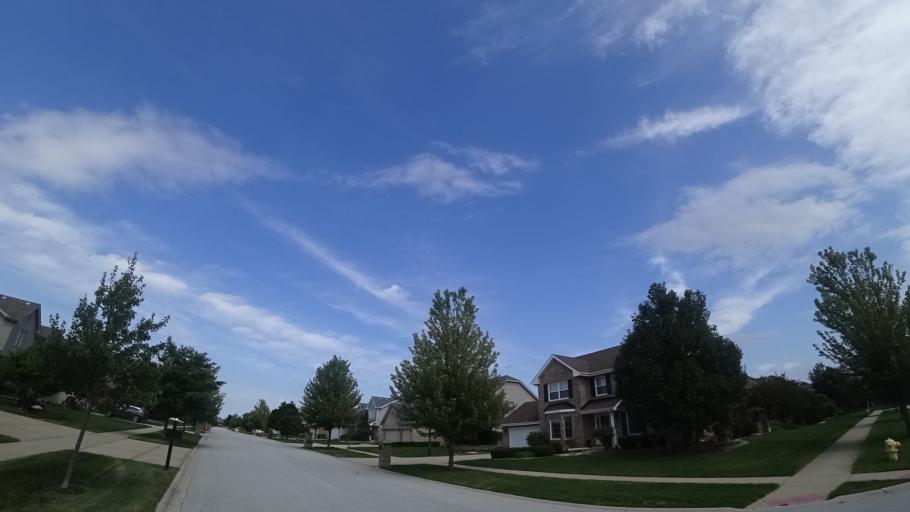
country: US
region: Illinois
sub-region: Cook County
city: Orland Hills
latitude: 41.5660
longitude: -87.8270
